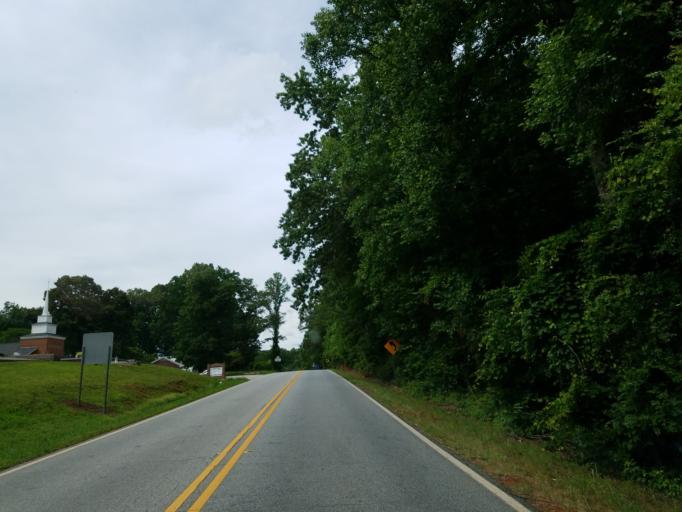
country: US
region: Georgia
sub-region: Lumpkin County
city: Dahlonega
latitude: 34.5722
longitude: -83.9677
